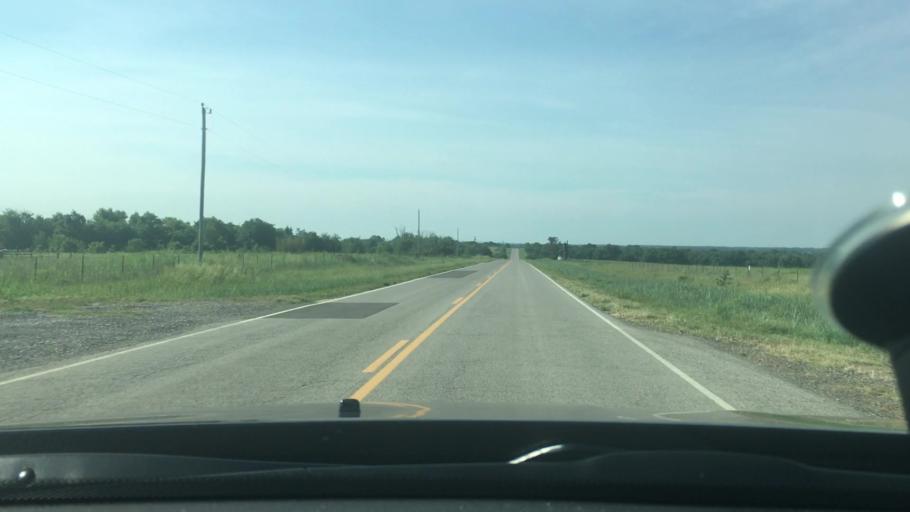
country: US
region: Oklahoma
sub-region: Garvin County
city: Maysville
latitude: 34.6623
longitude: -97.4053
